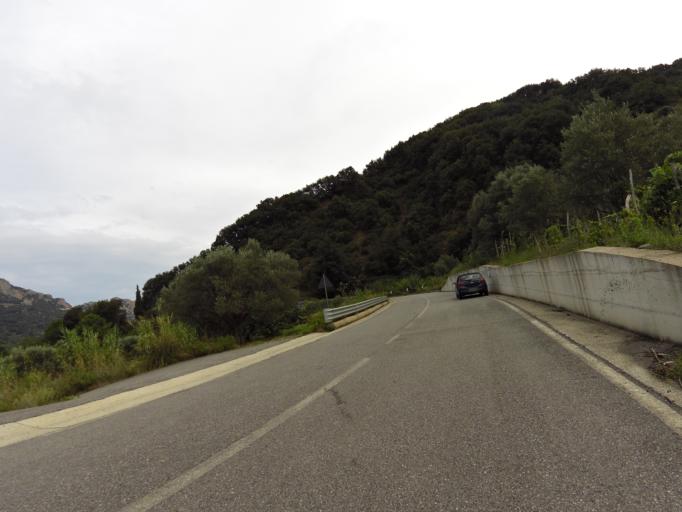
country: IT
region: Calabria
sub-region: Provincia di Reggio Calabria
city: Pazzano
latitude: 38.4429
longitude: 16.3994
